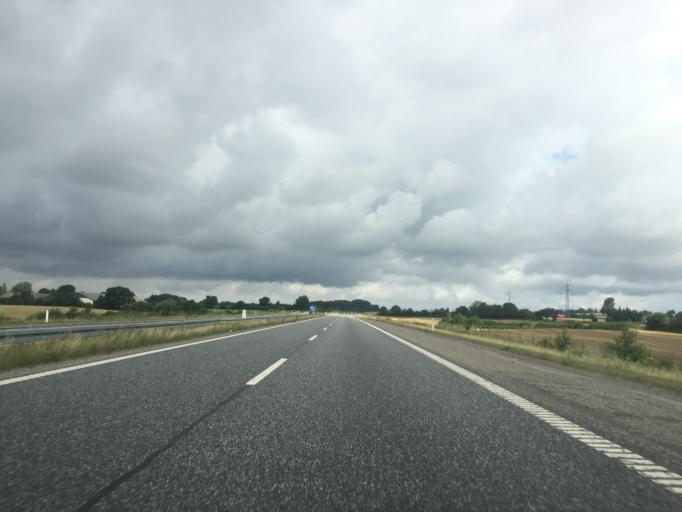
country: DK
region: South Denmark
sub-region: Svendborg Kommune
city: Svendborg
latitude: 55.1481
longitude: 10.5537
